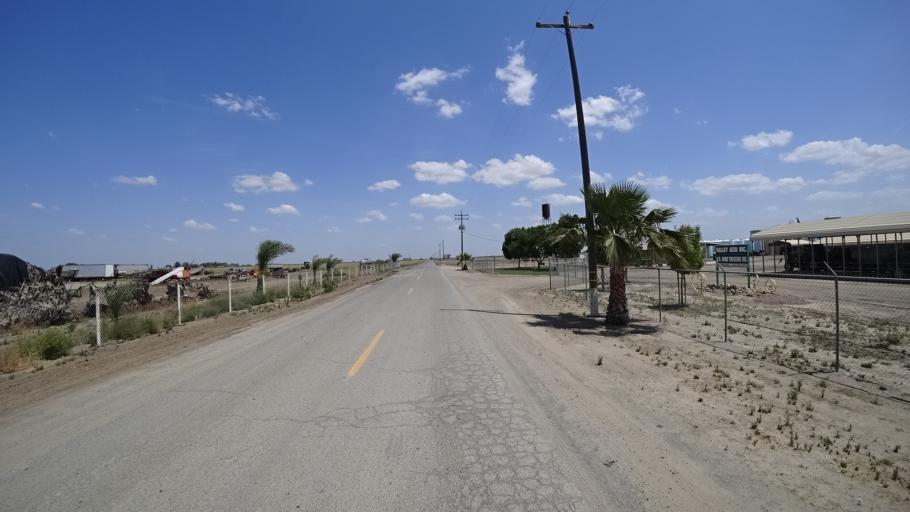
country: US
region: California
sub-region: Kings County
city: Stratford
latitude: 36.1821
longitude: -119.8244
